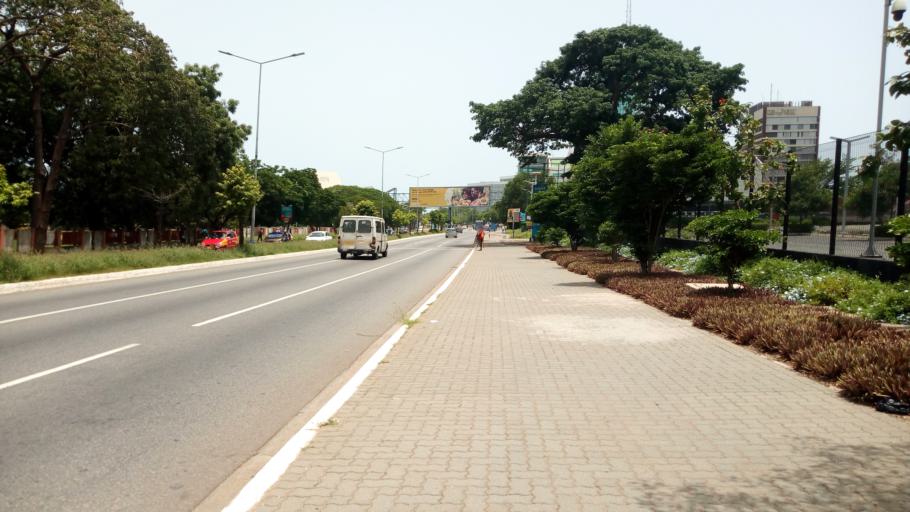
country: GH
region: Greater Accra
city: Accra
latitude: 5.5575
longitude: -0.1989
